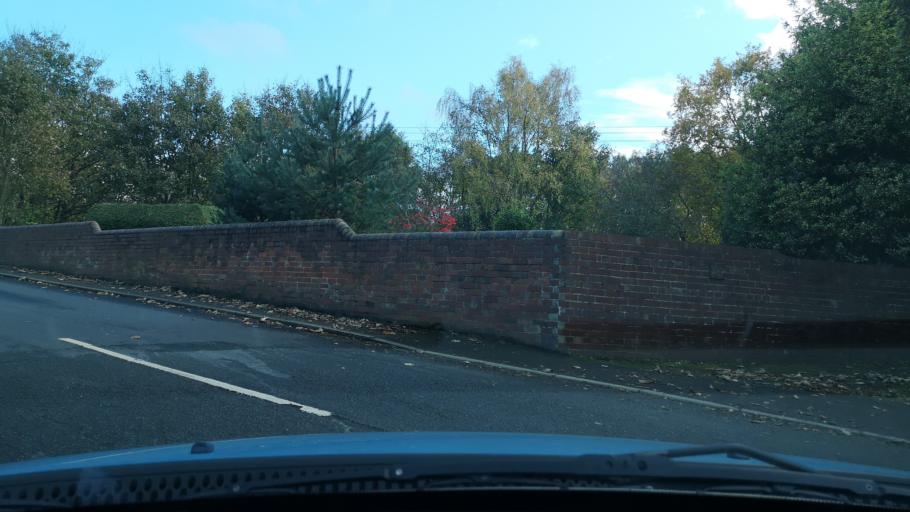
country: GB
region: England
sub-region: City and Borough of Wakefield
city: Ryhill
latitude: 53.6233
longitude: -1.4270
